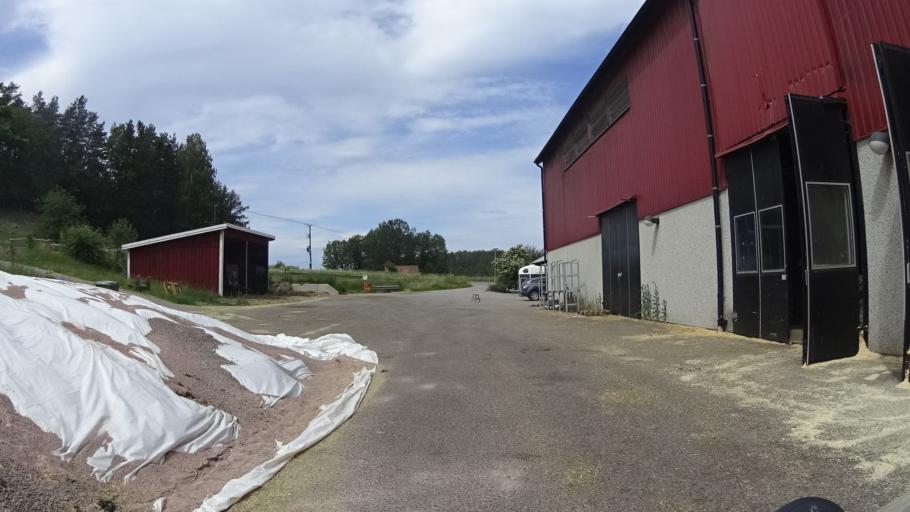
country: SE
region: Kalmar
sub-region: Vasterviks Kommun
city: Gamleby
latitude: 57.9131
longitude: 16.4037
